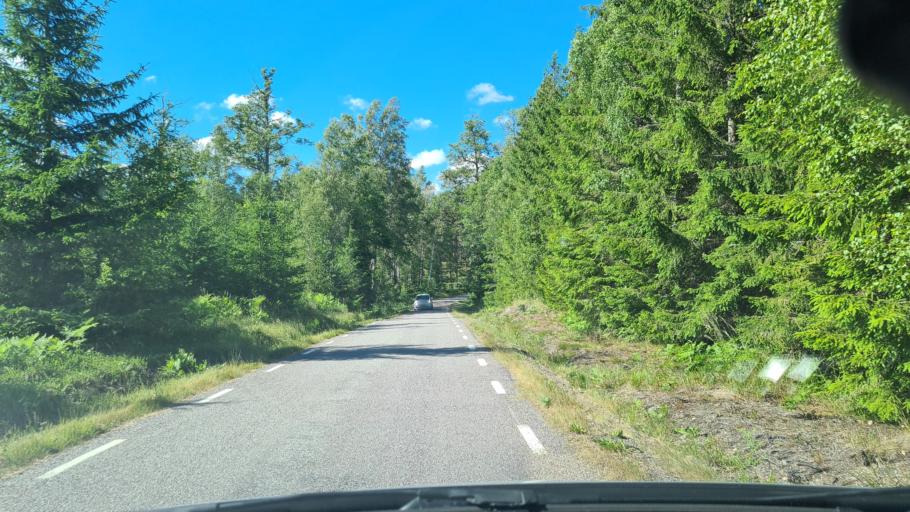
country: SE
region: OEstergoetland
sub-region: Norrkopings Kommun
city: Krokek
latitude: 58.7078
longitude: 16.4251
